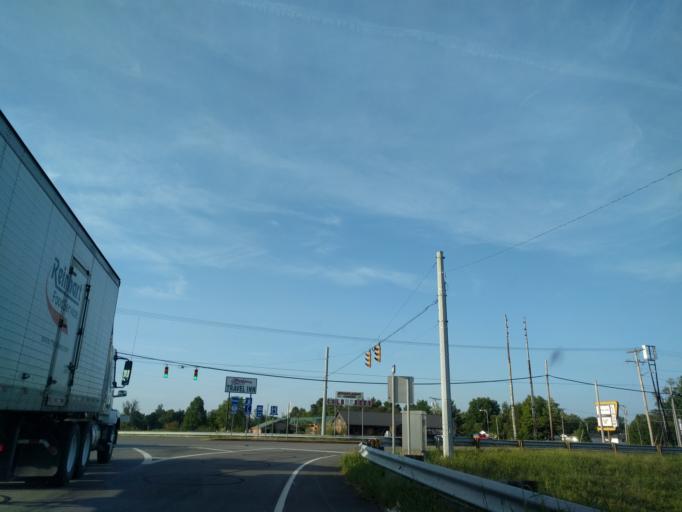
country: US
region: Indiana
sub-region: Scott County
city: Scottsburg
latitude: 38.6852
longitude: -85.7871
